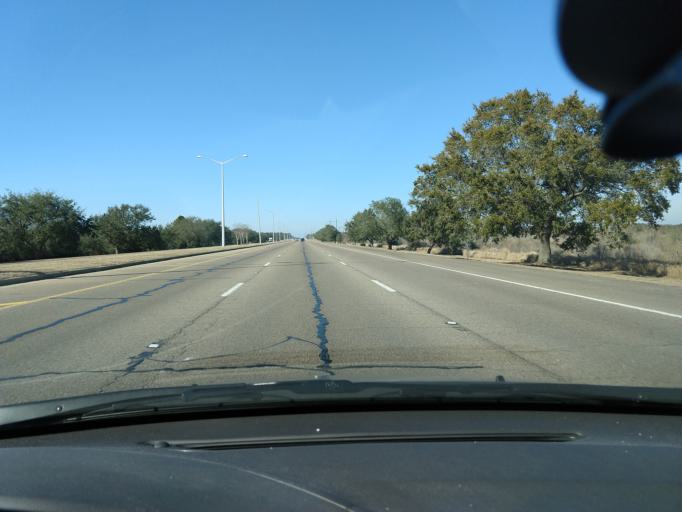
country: US
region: Mississippi
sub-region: Jackson County
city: Gautier
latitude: 30.3804
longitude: -88.5975
